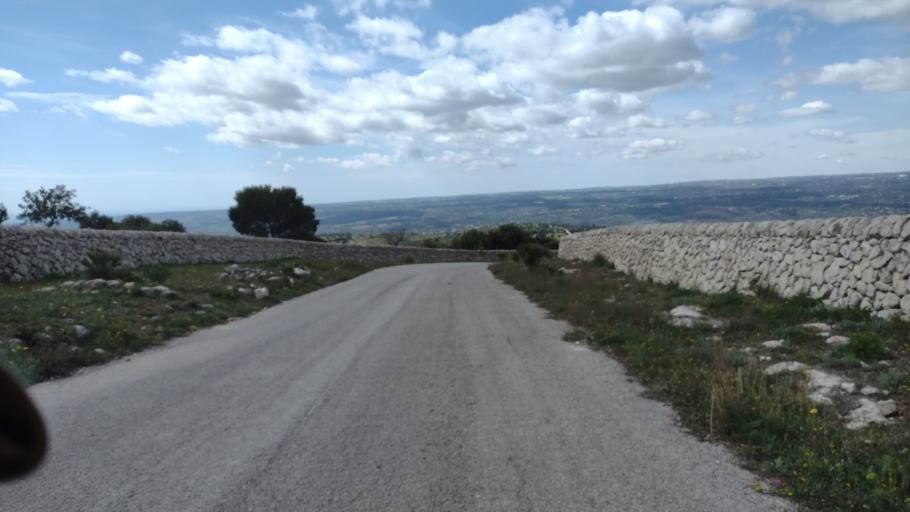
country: IT
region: Sicily
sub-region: Provincia di Siracusa
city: Noto
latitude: 36.9172
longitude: 14.9815
